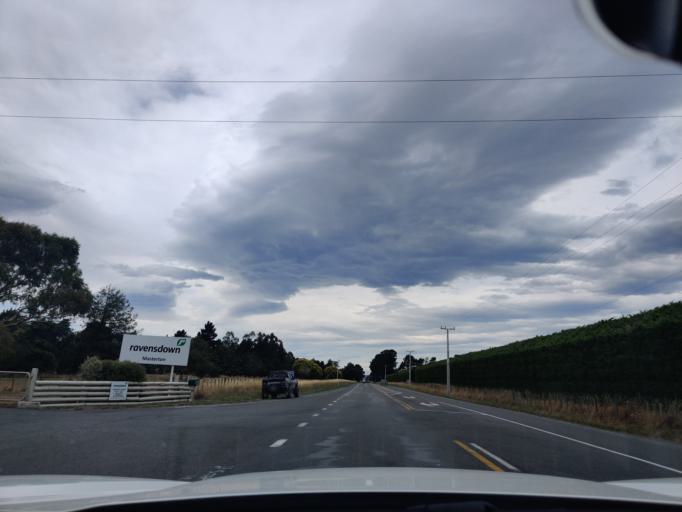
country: NZ
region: Wellington
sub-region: Masterton District
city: Masterton
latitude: -40.9885
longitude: 175.5739
